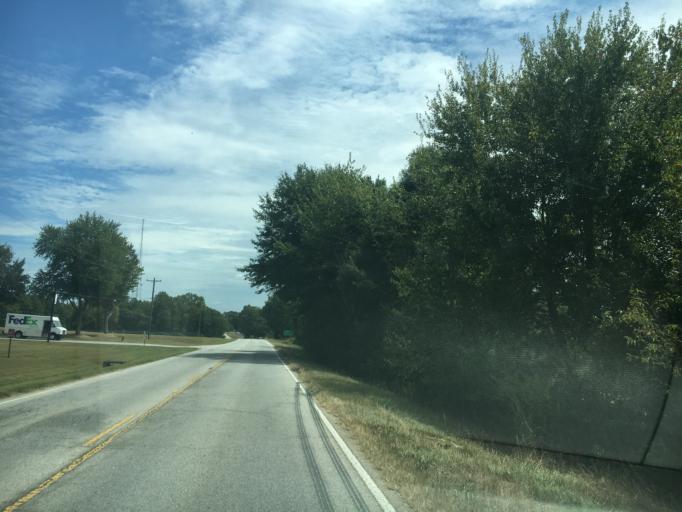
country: US
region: South Carolina
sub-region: Laurens County
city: Laurens
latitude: 34.5345
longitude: -82.0581
